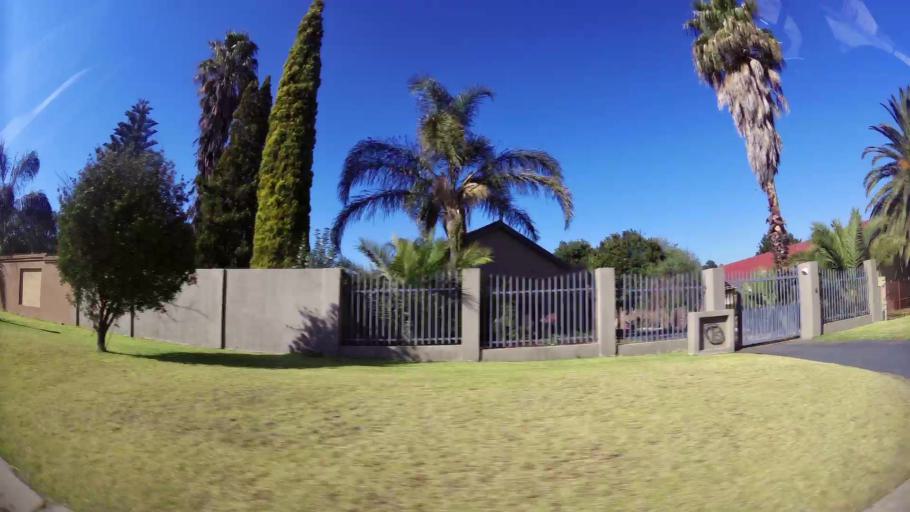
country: ZA
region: Mpumalanga
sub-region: Nkangala District Municipality
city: Witbank
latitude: -25.8873
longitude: 29.2494
